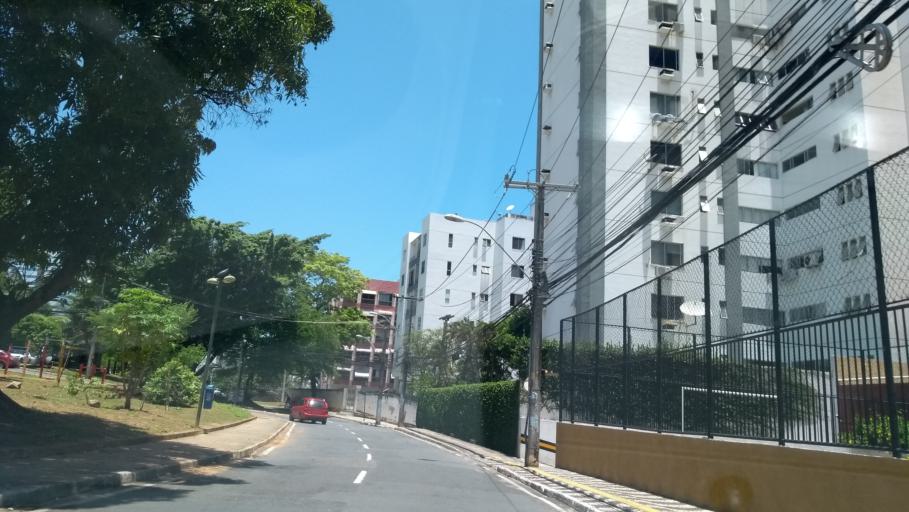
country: BR
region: Bahia
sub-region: Salvador
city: Salvador
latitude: -12.9909
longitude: -38.4518
